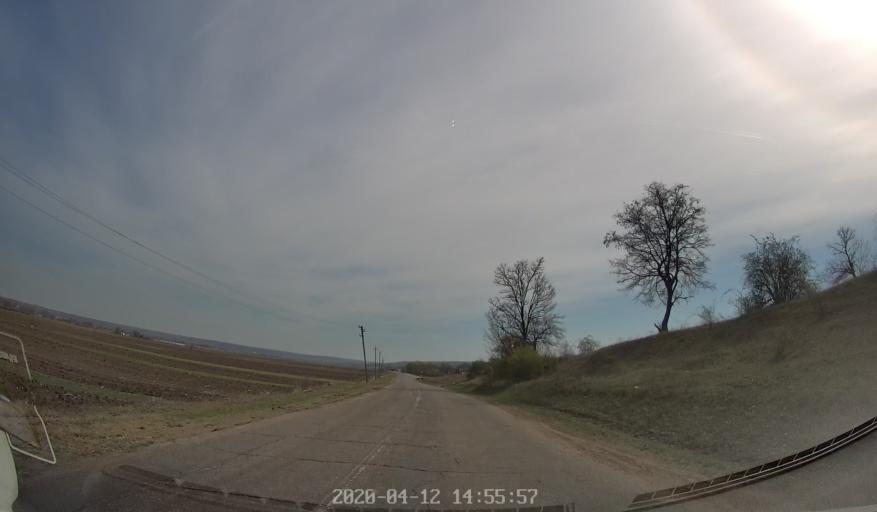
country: MD
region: Telenesti
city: Dubasari
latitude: 47.2660
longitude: 29.1258
